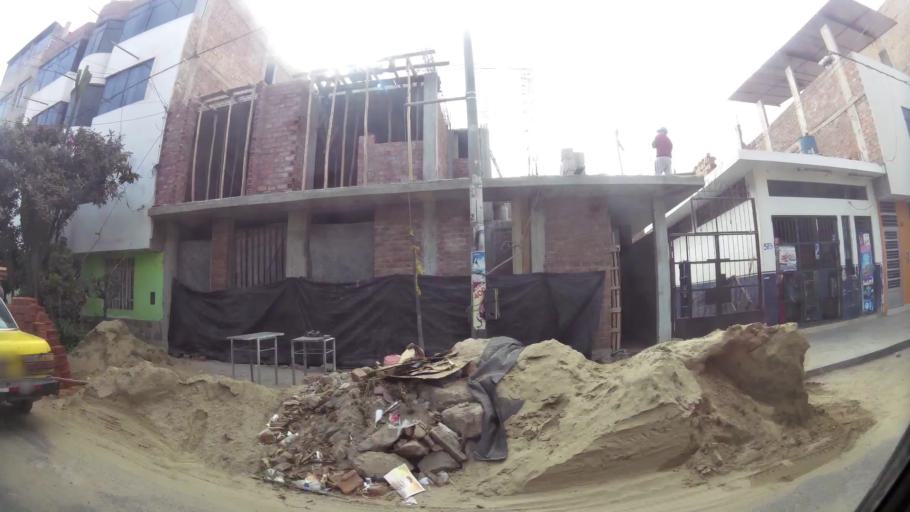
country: PE
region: La Libertad
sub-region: Provincia de Trujillo
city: El Porvenir
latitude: -8.1010
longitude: -79.0131
